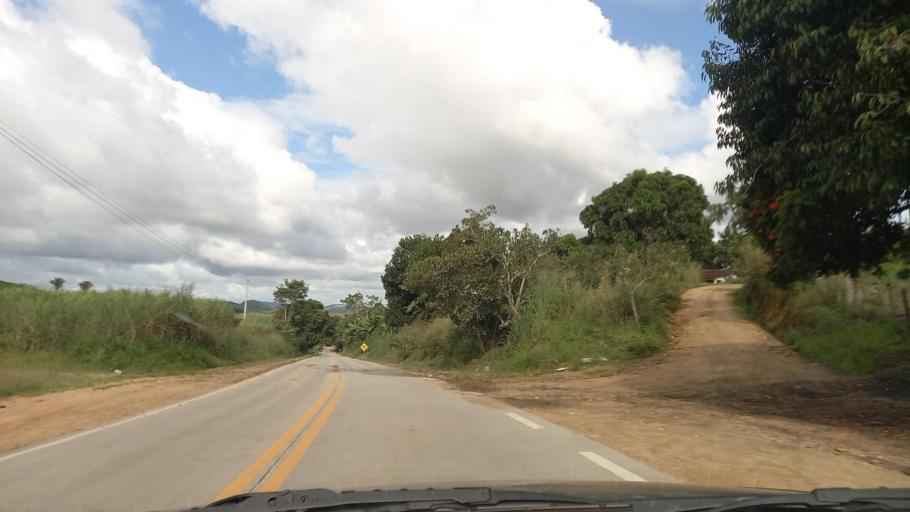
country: BR
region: Pernambuco
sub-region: Maraial
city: Maraial
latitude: -8.7891
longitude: -35.8960
